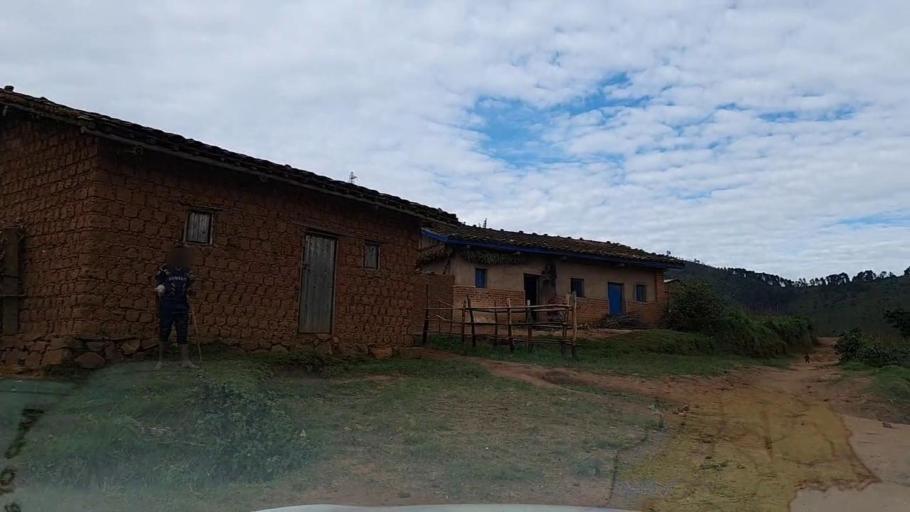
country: RW
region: Southern Province
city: Nzega
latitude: -2.4081
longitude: 29.4941
